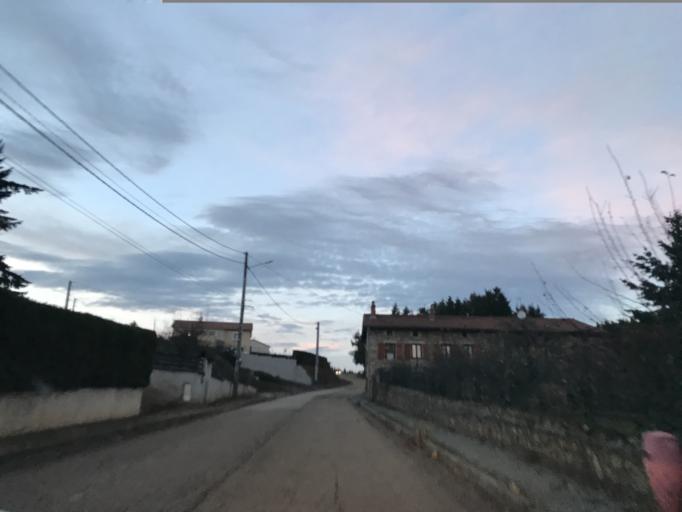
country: FR
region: Rhone-Alpes
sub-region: Departement de la Loire
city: Noiretable
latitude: 45.8225
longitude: 3.7644
